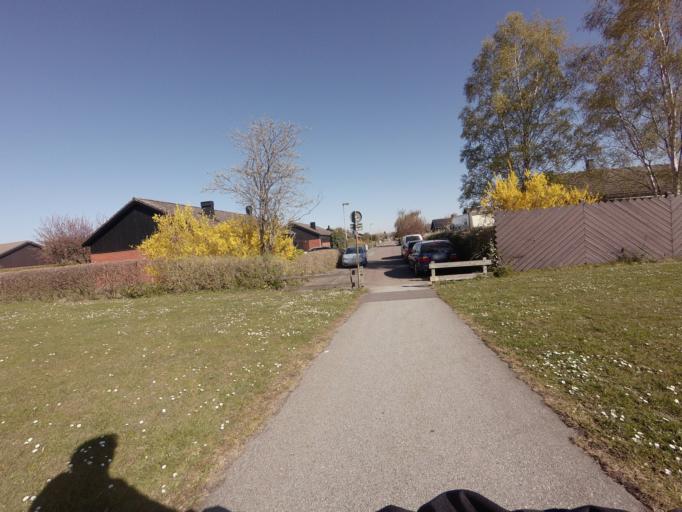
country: SE
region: Skane
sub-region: Lomma Kommun
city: Lomma
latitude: 55.6695
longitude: 13.0942
